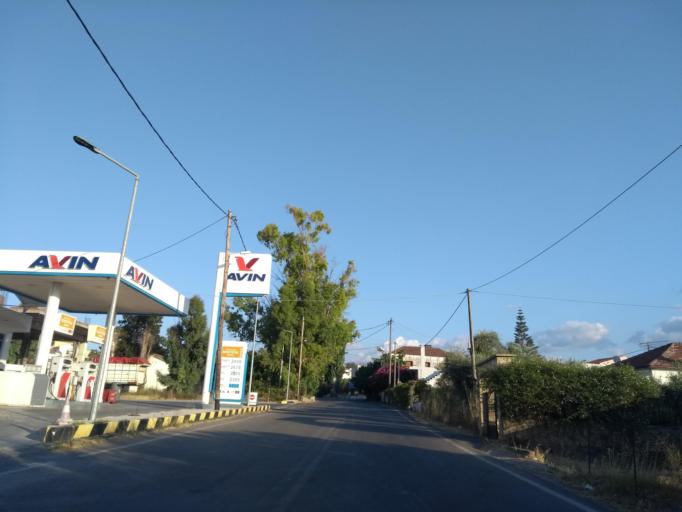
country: GR
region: Crete
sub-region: Nomos Chanias
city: Kalivai
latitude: 35.4115
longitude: 24.1960
